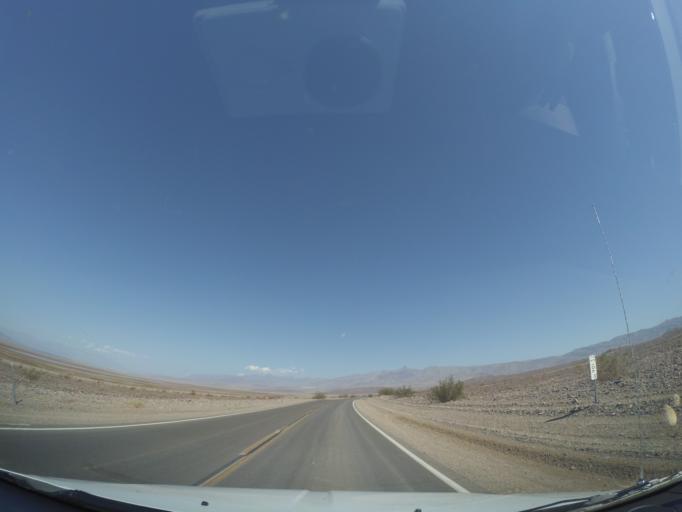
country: US
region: Nevada
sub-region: Nye County
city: Beatty
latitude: 36.5133
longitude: -116.8816
